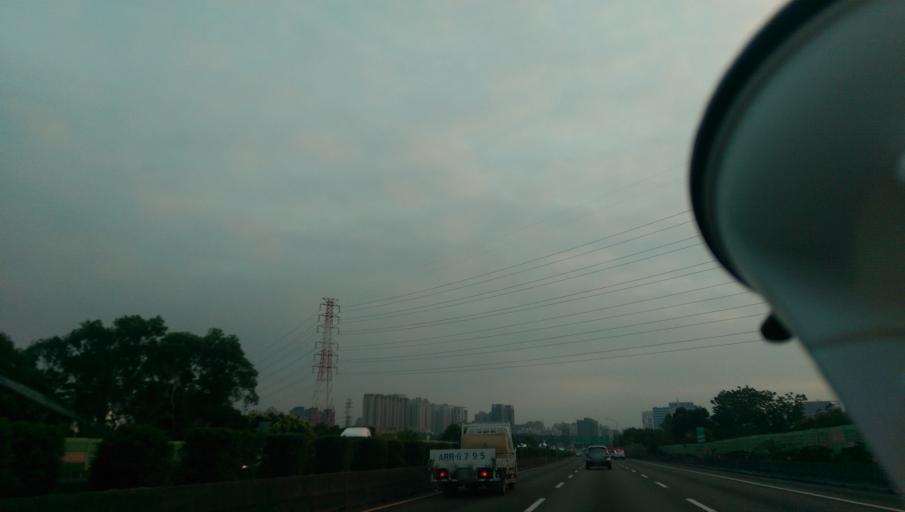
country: TW
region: Taiwan
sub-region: Hsinchu
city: Zhubei
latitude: 24.8076
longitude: 121.0102
